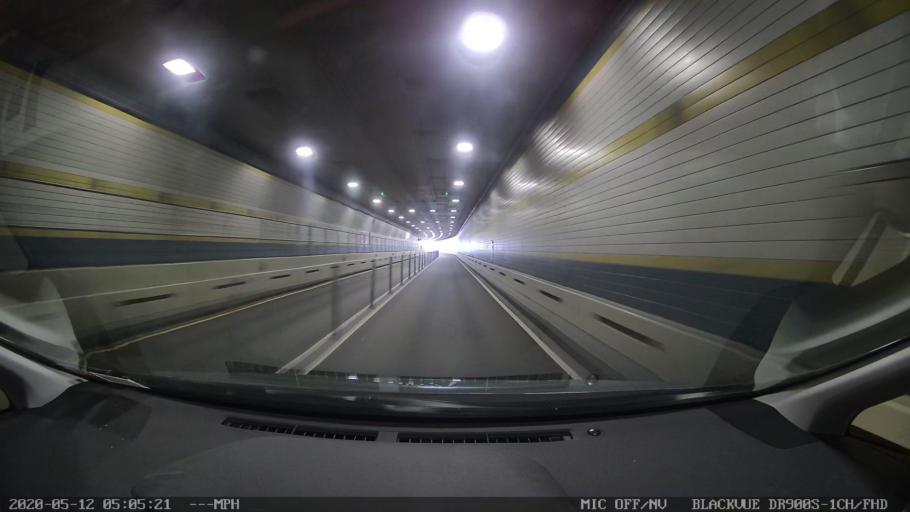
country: US
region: New York
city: New York City
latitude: 40.6844
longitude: -74.0070
